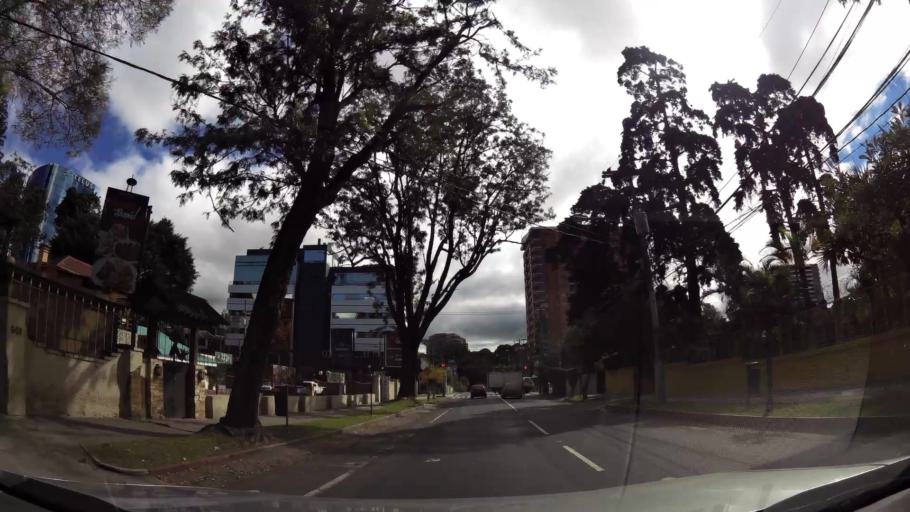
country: GT
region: Guatemala
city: Santa Catarina Pinula
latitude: 14.6003
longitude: -90.5114
